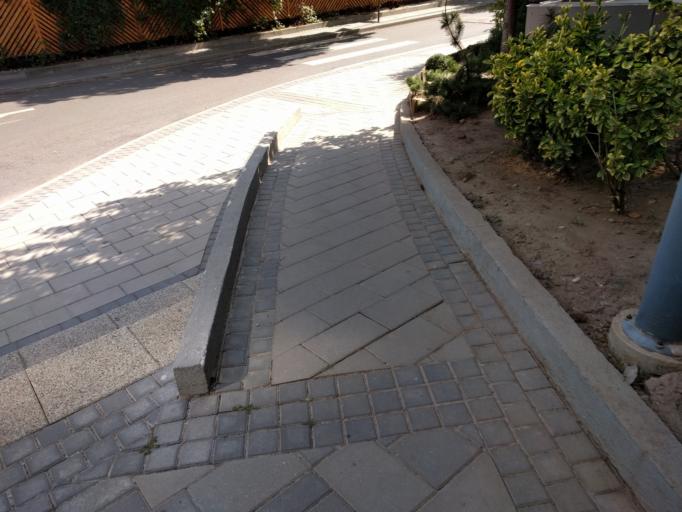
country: RO
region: Bucuresti
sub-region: Municipiul Bucuresti
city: Bucharest
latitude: 44.4236
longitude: 26.1410
